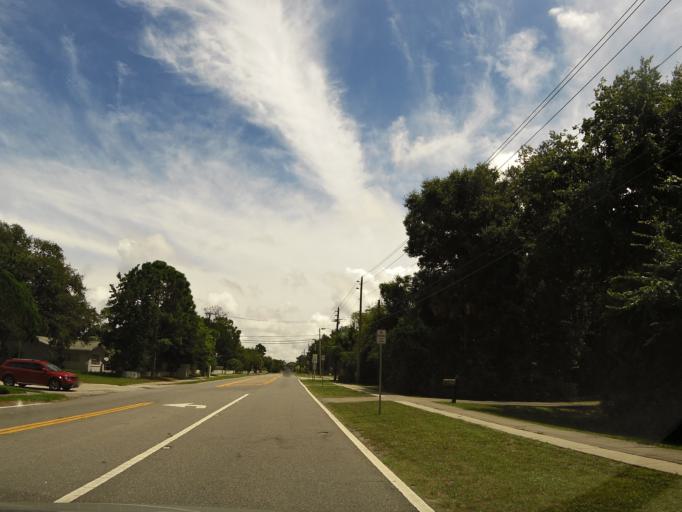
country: US
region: Florida
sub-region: Brevard County
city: Mims
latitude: 28.6372
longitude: -80.8531
